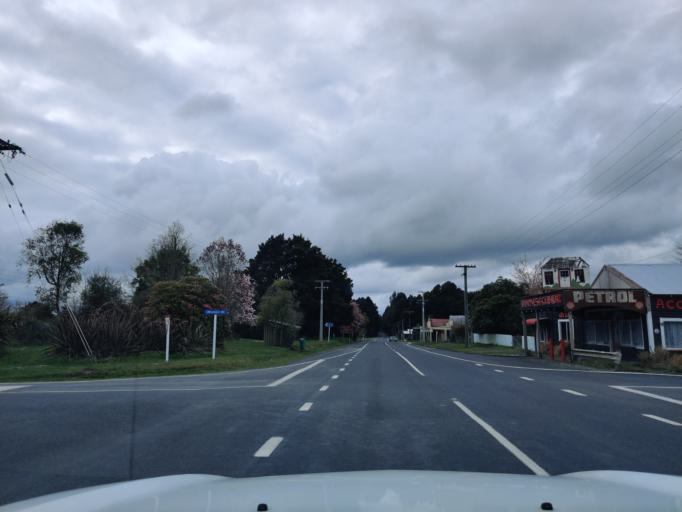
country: NZ
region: Waikato
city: Turangi
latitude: -38.9996
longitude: 175.3774
